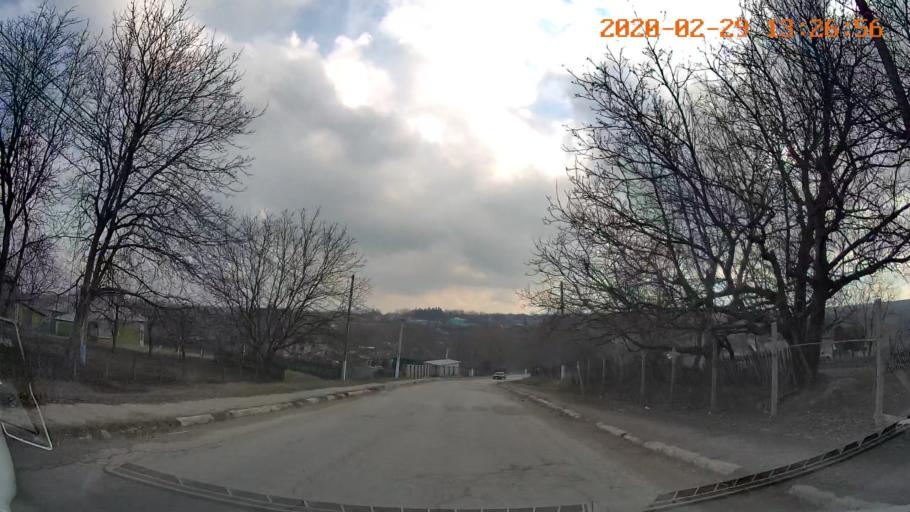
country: MD
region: Telenesti
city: Camenca
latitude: 47.9159
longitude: 28.6398
